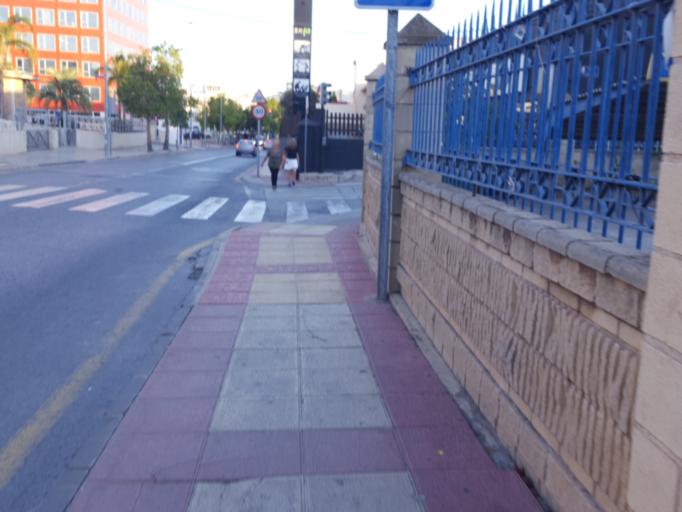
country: ES
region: Murcia
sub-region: Murcia
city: Murcia
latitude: 38.0061
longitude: -1.1496
